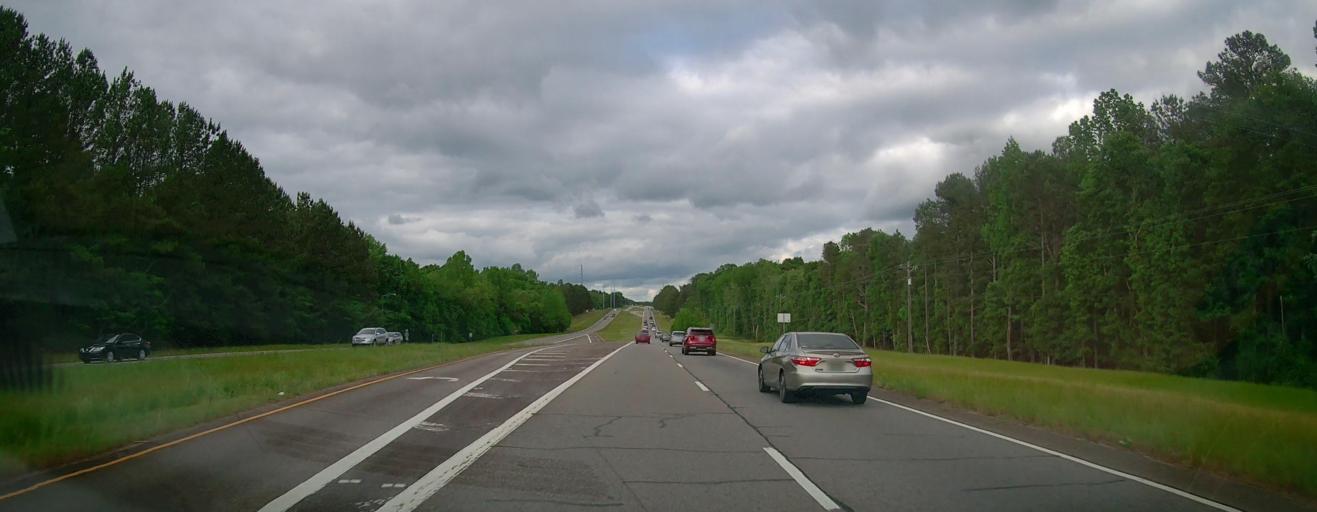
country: US
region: Georgia
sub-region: Oconee County
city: Bogart
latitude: 33.9058
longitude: -83.5662
